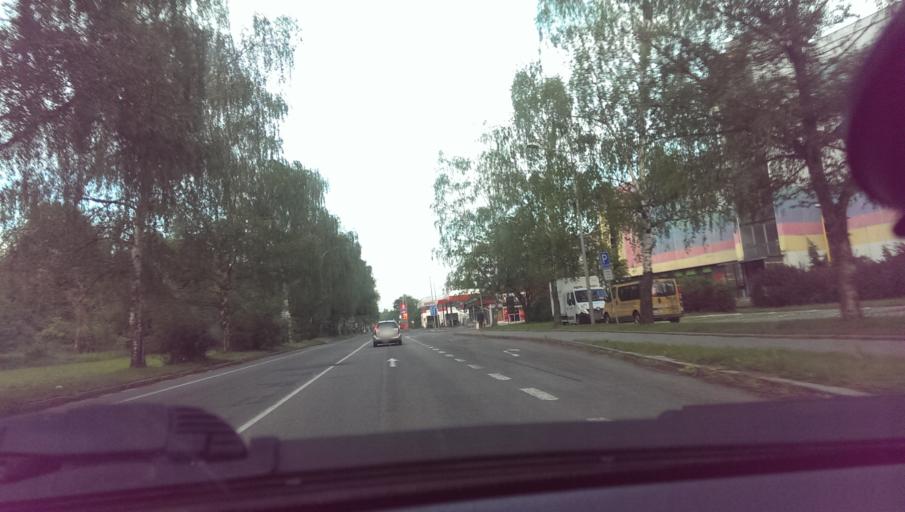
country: CZ
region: Zlin
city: Valasske Mezirici
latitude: 49.4771
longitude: 17.9839
